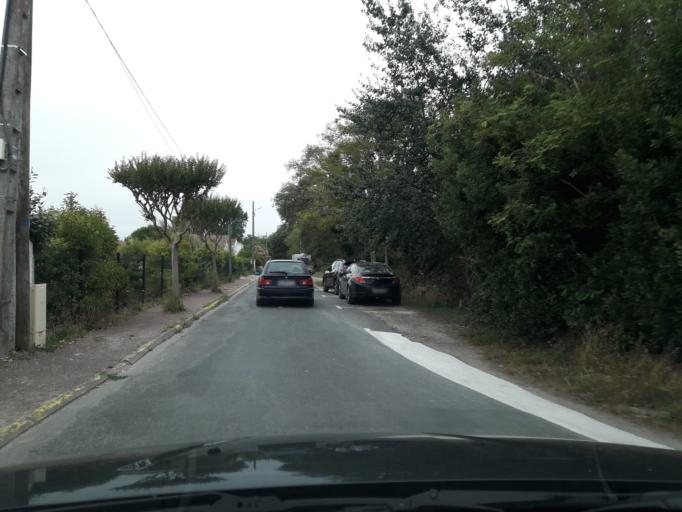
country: FR
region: Poitou-Charentes
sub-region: Departement de la Charente-Maritime
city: Boyard-Ville
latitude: 45.9696
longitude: -1.2388
